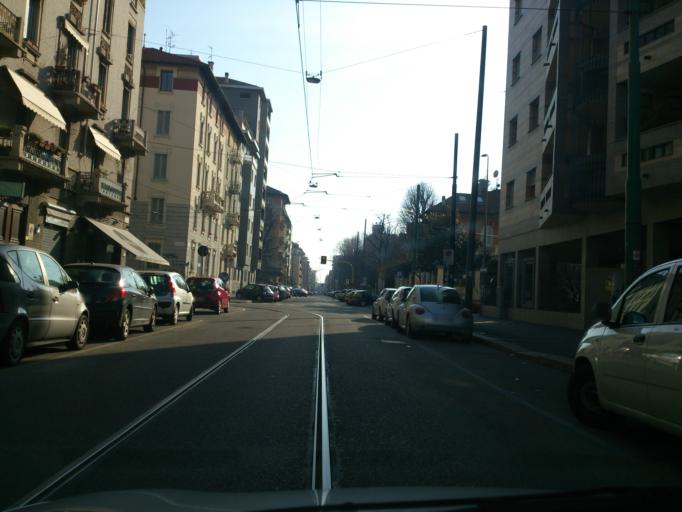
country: IT
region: Lombardy
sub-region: Citta metropolitana di Milano
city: Milano
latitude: 45.4544
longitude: 9.2133
